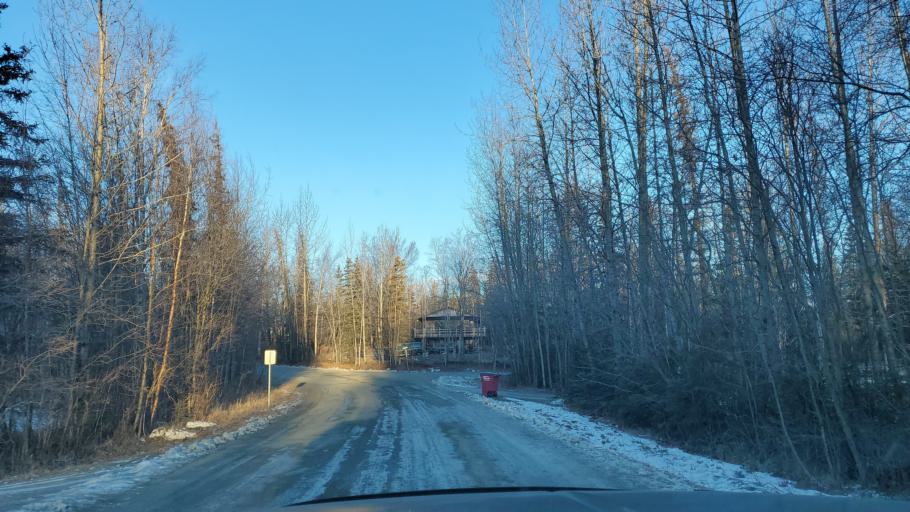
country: US
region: Alaska
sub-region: Matanuska-Susitna Borough
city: Tanaina
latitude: 61.6085
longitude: -149.4038
